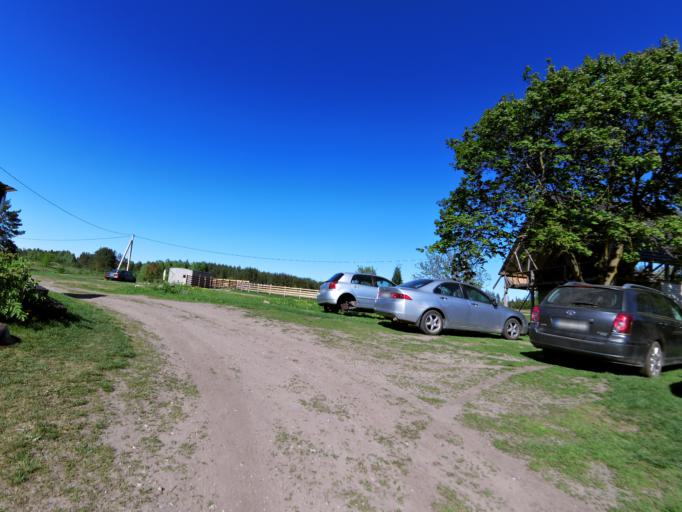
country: LT
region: Vilnius County
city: Pilaite
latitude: 54.6828
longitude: 25.1620
